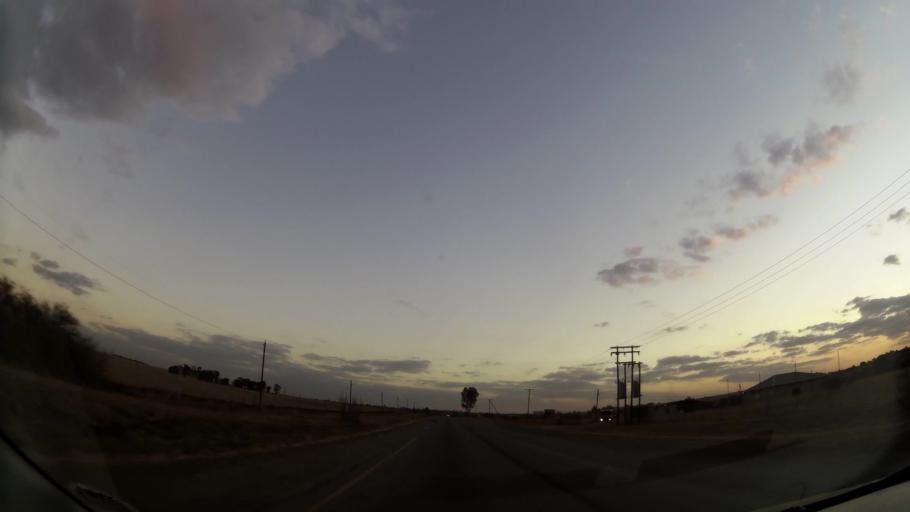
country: ZA
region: Gauteng
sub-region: West Rand District Municipality
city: Krugersdorp
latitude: -26.0546
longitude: 27.7077
